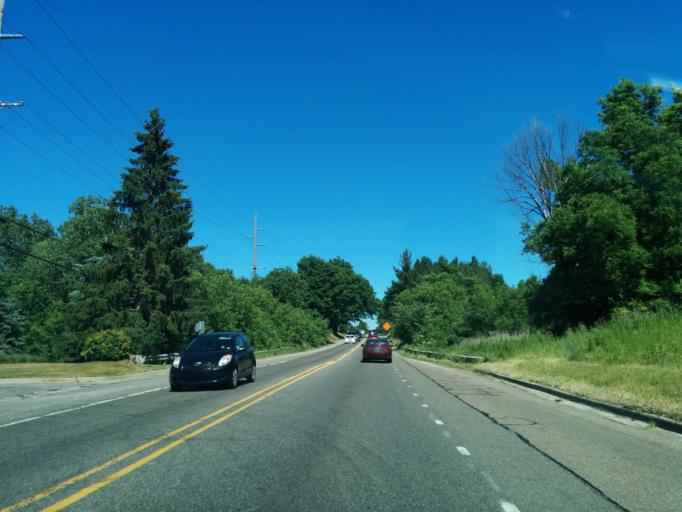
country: US
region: Michigan
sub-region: Oakland County
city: Wolverine Lake
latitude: 42.5409
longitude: -83.4348
